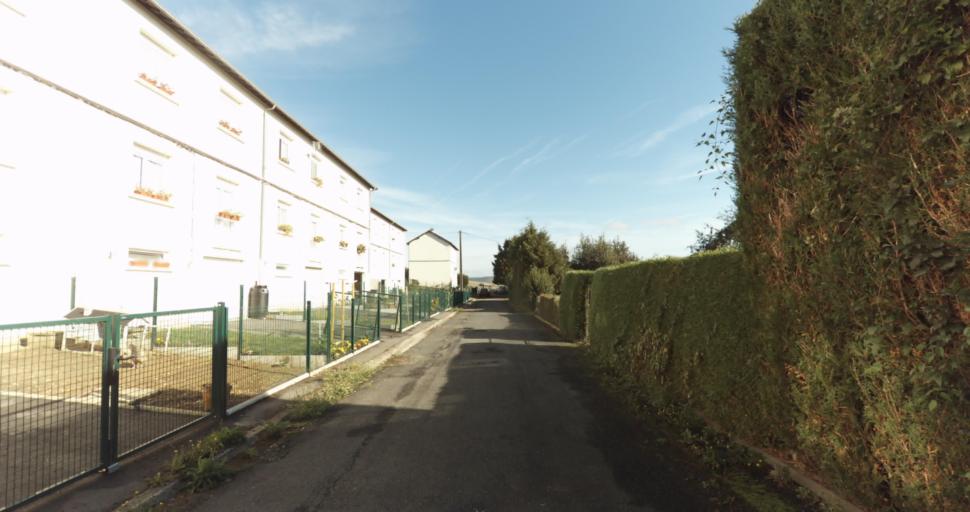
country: FR
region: Lower Normandy
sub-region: Departement de l'Orne
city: Vimoutiers
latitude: 48.9312
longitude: 0.2662
